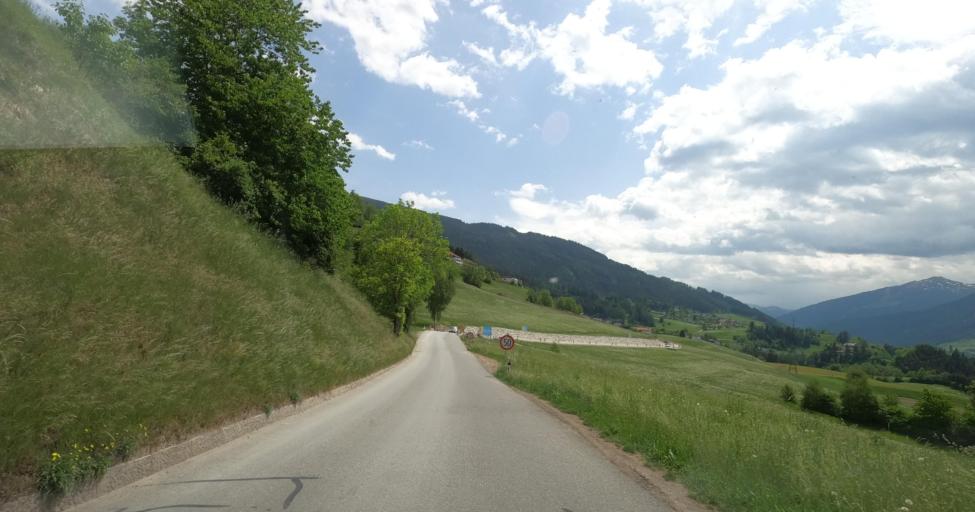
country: AT
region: Tyrol
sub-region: Politischer Bezirk Innsbruck Land
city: Pfons
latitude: 47.1485
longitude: 11.4557
